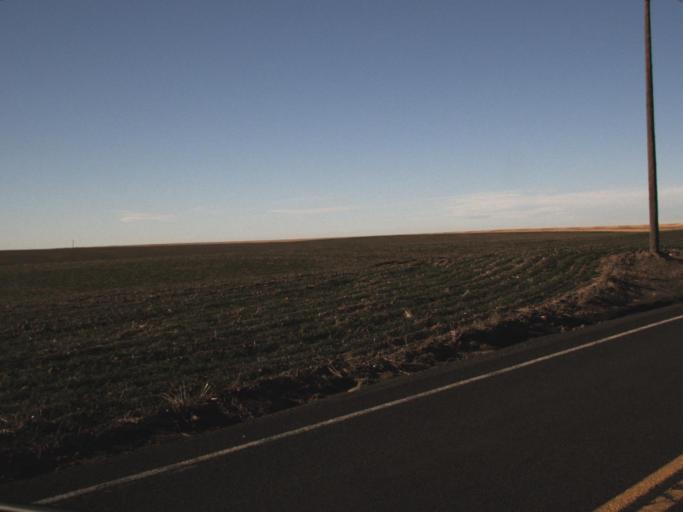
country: US
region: Washington
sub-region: Adams County
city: Ritzville
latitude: 47.0978
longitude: -118.3655
